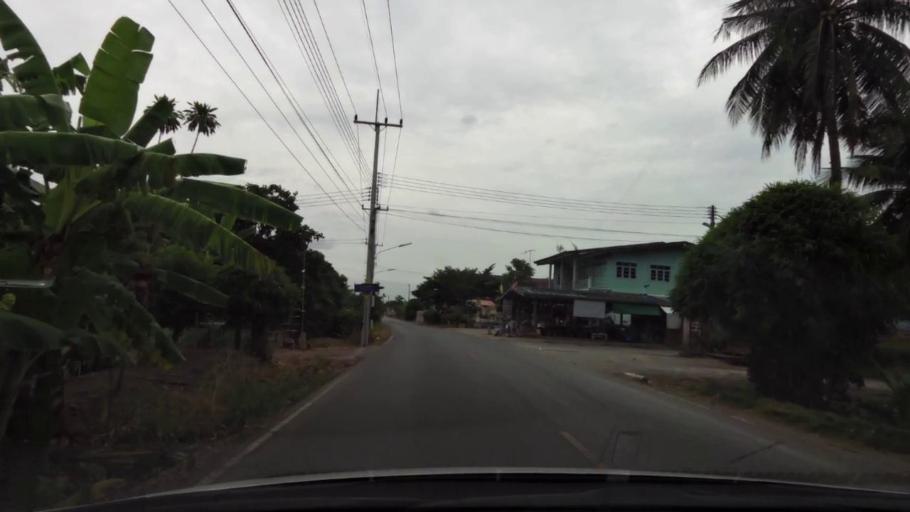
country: TH
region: Ratchaburi
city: Damnoen Saduak
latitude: 13.5747
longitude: 99.9951
